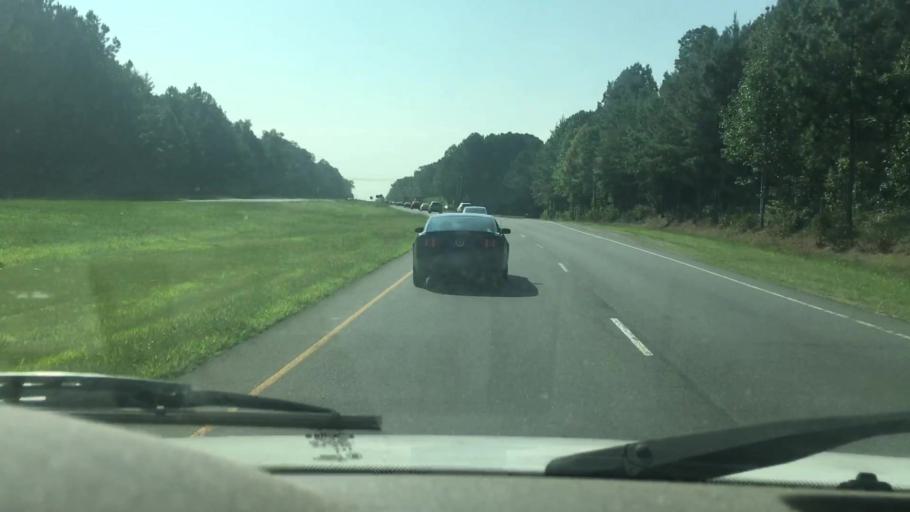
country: US
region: North Carolina
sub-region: Gaston County
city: Mount Holly
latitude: 35.3397
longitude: -80.9651
